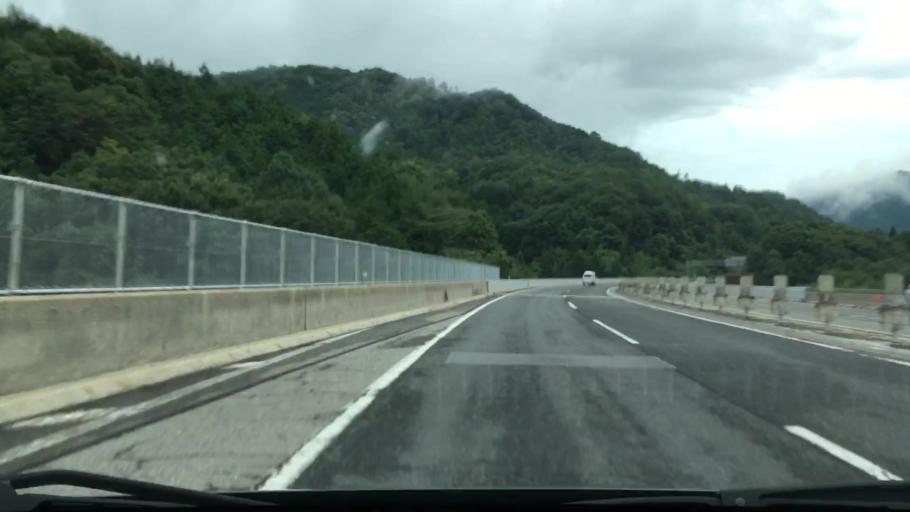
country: JP
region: Hiroshima
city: Hiroshima-shi
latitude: 34.5688
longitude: 132.4563
